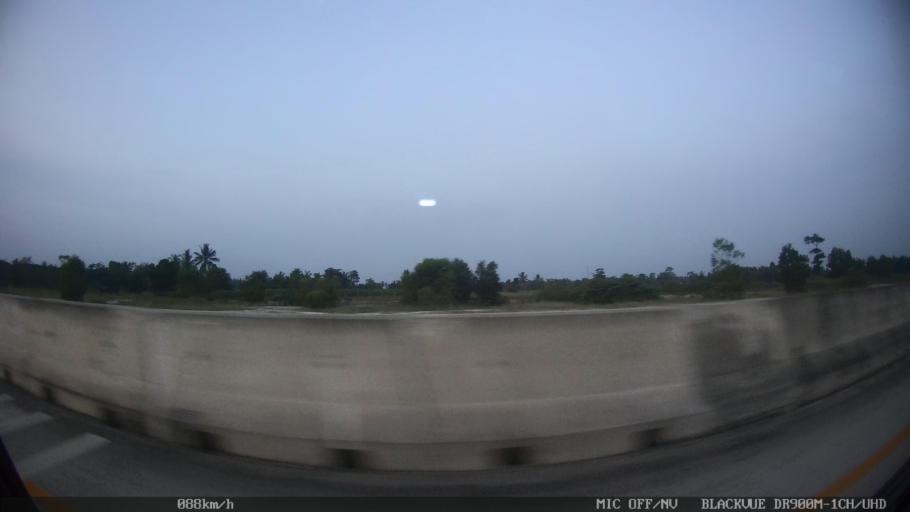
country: ID
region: Lampung
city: Sidorejo
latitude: -5.6421
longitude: 105.5738
